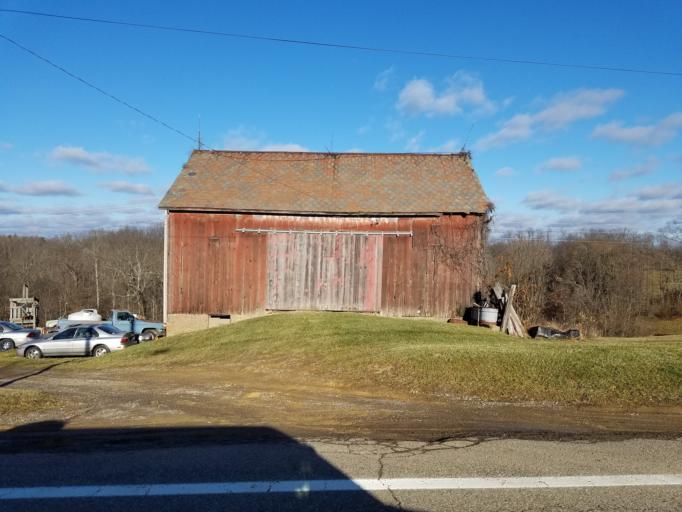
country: US
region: Ohio
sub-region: Coshocton County
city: Coshocton
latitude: 40.2534
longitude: -81.9516
